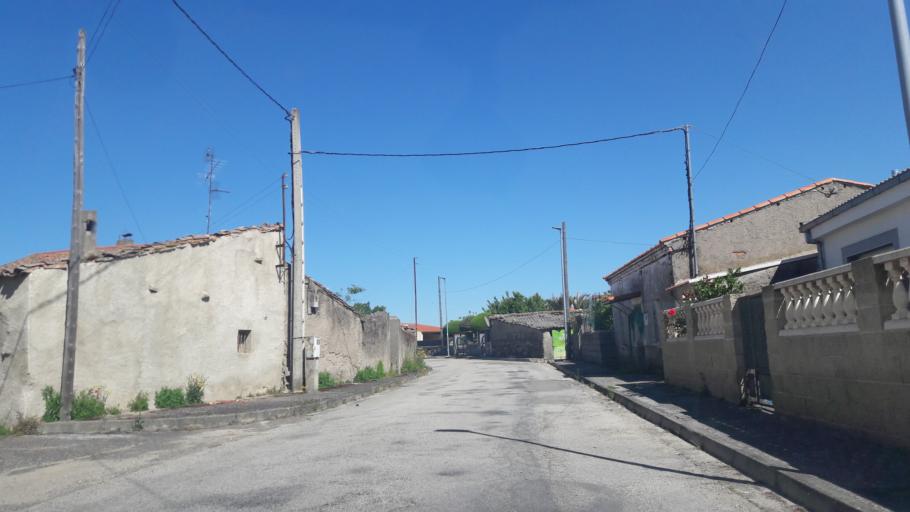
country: ES
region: Castille and Leon
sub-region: Provincia de Salamanca
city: Banobarez
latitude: 40.8518
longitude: -6.6142
